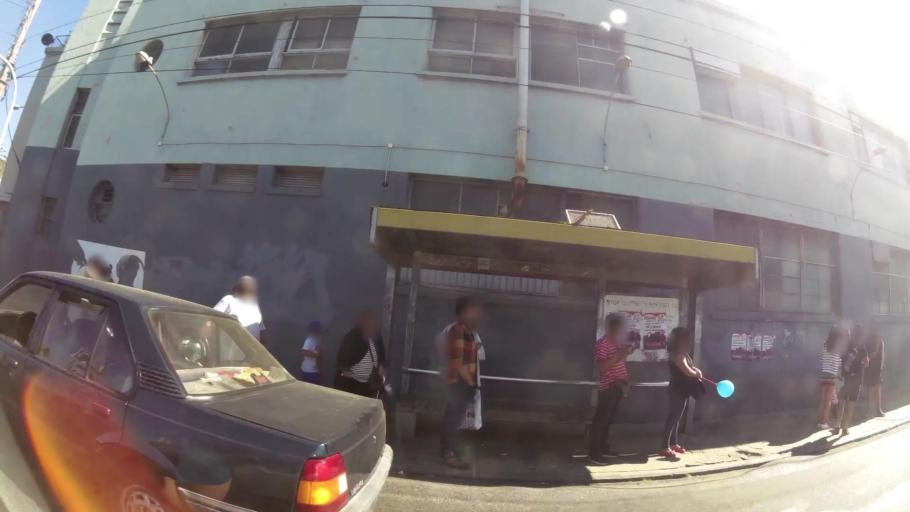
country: CL
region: Valparaiso
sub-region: Provincia de Valparaiso
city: Valparaiso
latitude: -33.0443
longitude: -71.6123
